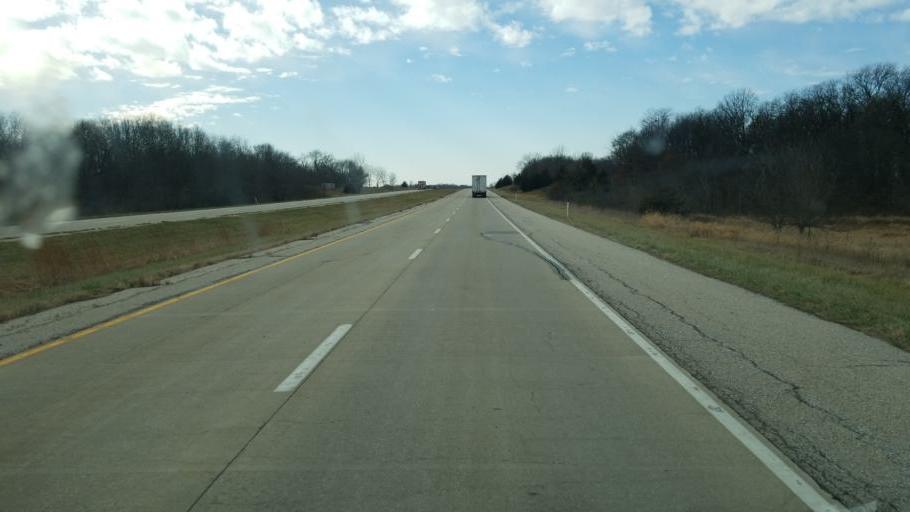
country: US
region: Illinois
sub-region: Knox County
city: Galesburg
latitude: 40.9296
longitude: -90.4283
